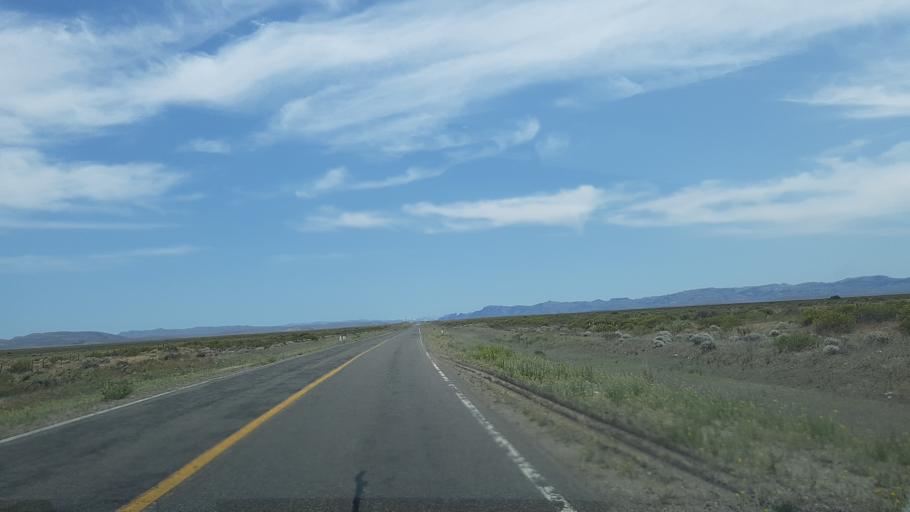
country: AR
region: Rio Negro
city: Pilcaniyeu
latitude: -40.5354
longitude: -70.7132
